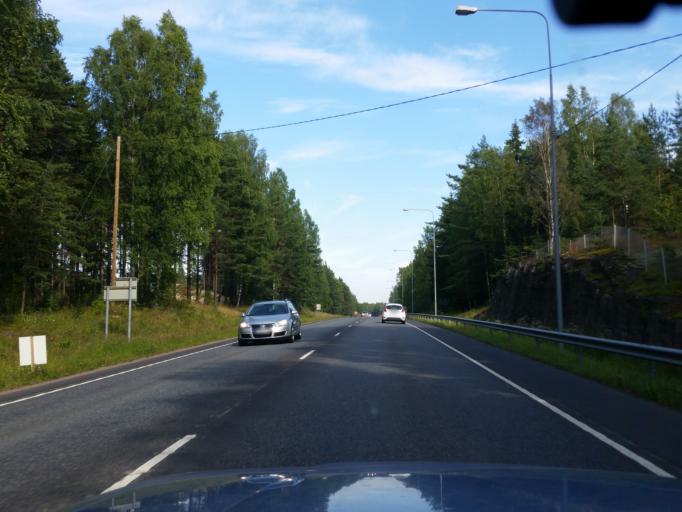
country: FI
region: Uusimaa
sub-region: Helsinki
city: Siuntio
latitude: 60.0990
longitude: 24.3072
